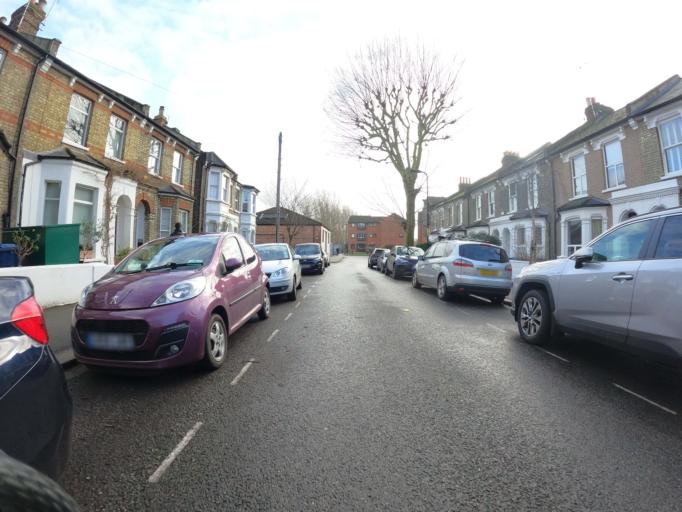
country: GB
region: England
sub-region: Greater London
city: Acton
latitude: 51.5054
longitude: -0.2621
